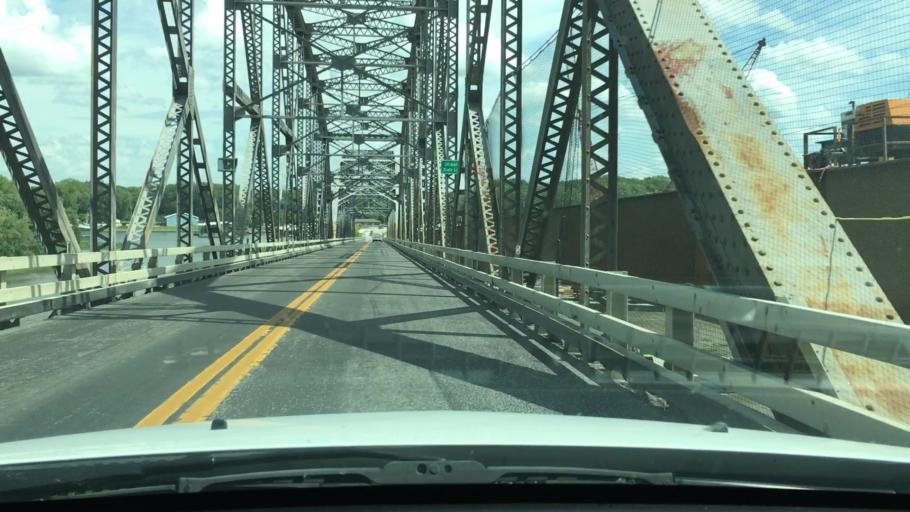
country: US
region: Missouri
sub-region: Pike County
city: Louisiana
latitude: 39.4573
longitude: -91.0463
